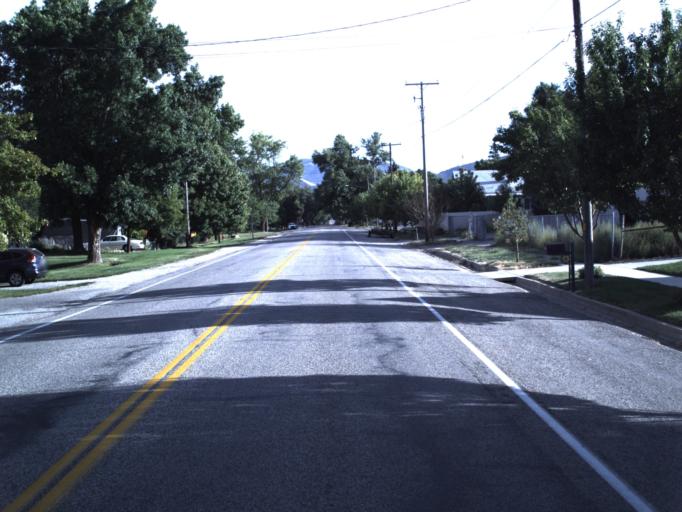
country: US
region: Utah
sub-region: Cache County
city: Wellsville
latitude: 41.6422
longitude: -111.9343
